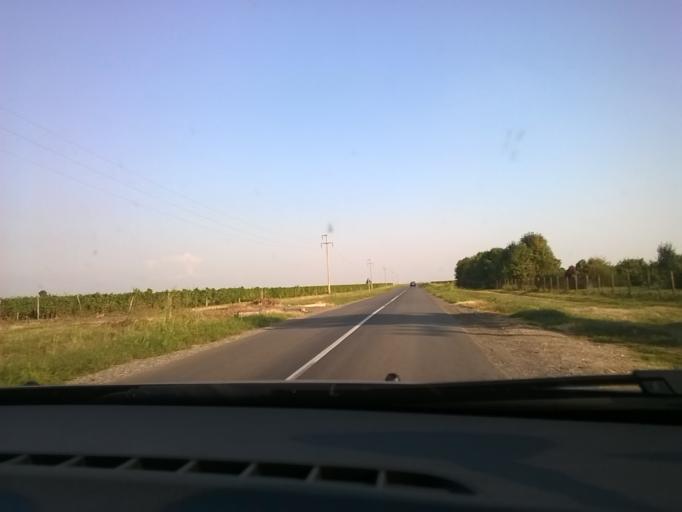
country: RS
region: Autonomna Pokrajina Vojvodina
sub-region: Juznobanatski Okrug
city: Vrsac
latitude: 45.1052
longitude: 21.3181
